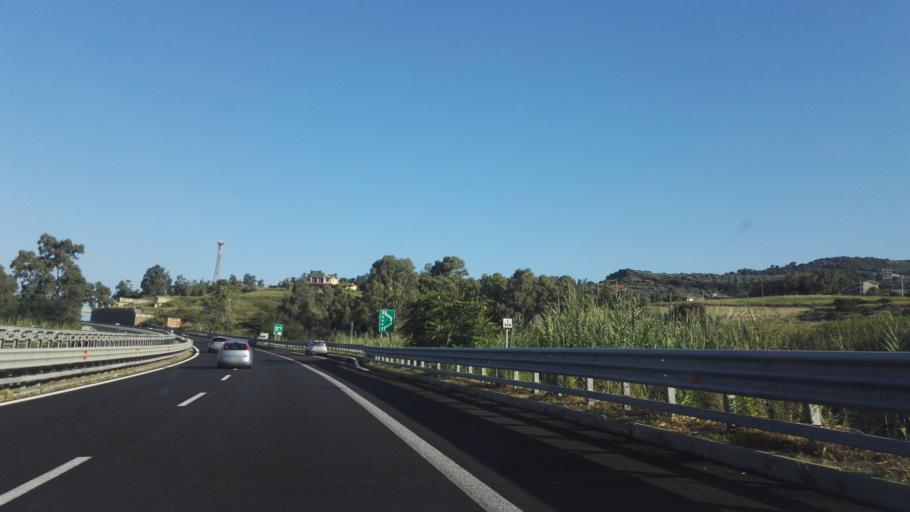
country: IT
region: Calabria
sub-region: Provincia di Catanzaro
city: Falerna Scalo
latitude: 38.9735
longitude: 16.1519
